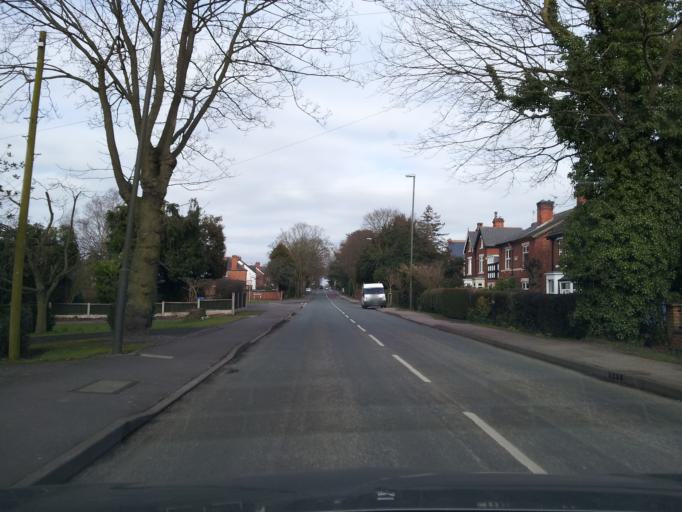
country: GB
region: England
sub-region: Derbyshire
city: Findern
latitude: 52.9129
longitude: -1.5433
